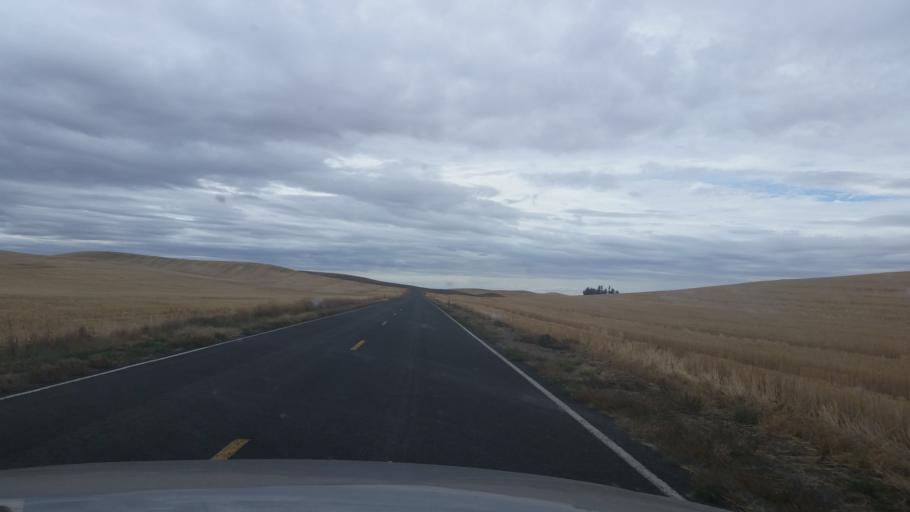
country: US
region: Washington
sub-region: Spokane County
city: Medical Lake
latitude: 47.5263
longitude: -117.8585
